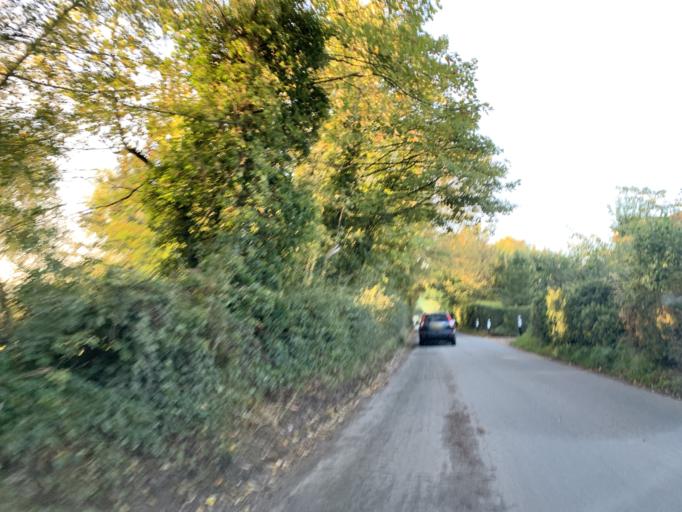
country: GB
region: England
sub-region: Wiltshire
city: Woodford
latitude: 51.1236
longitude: -1.8300
